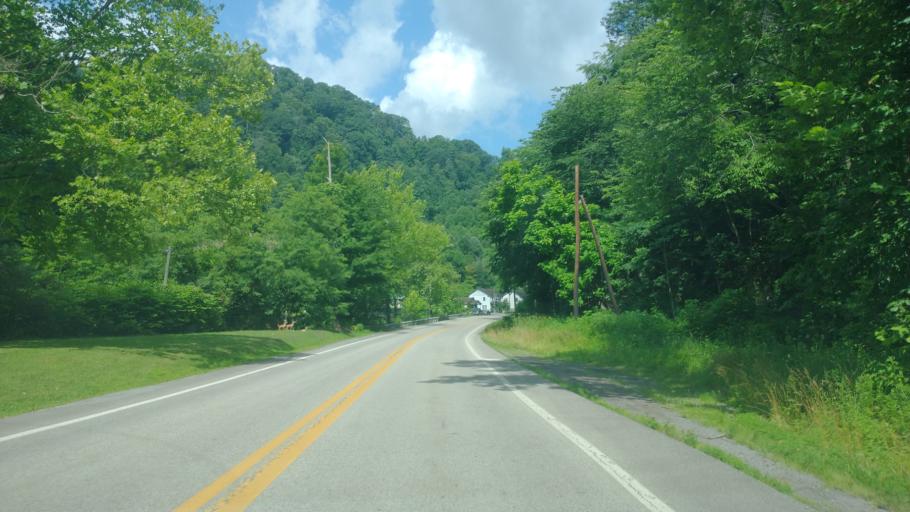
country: US
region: West Virginia
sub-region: McDowell County
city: Welch
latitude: 37.4139
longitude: -81.4810
